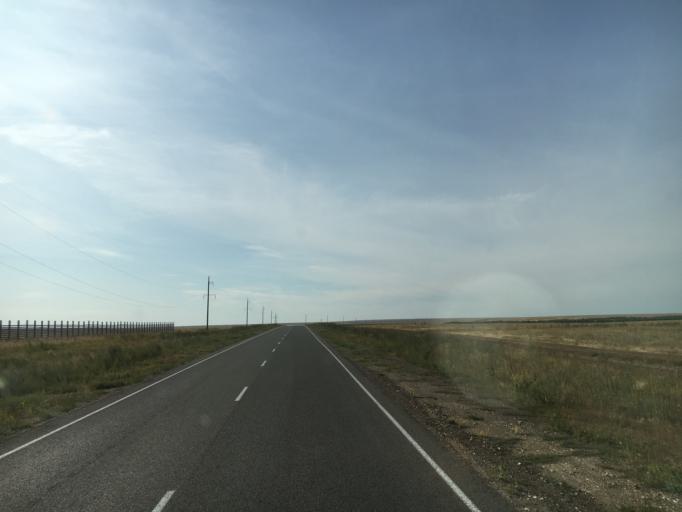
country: KZ
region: Batys Qazaqstan
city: Kamenka
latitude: 51.1445
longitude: 50.0952
